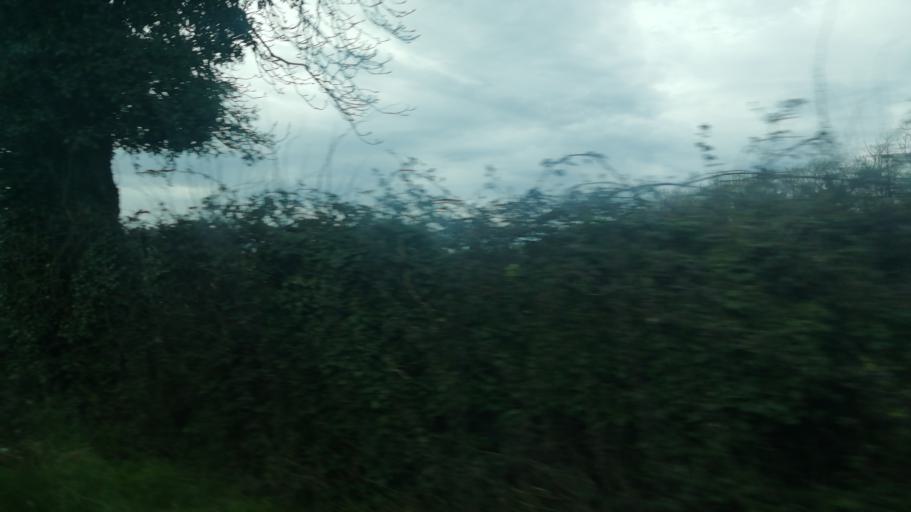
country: IE
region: Leinster
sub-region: Kildare
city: Clane
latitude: 53.3157
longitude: -6.7098
